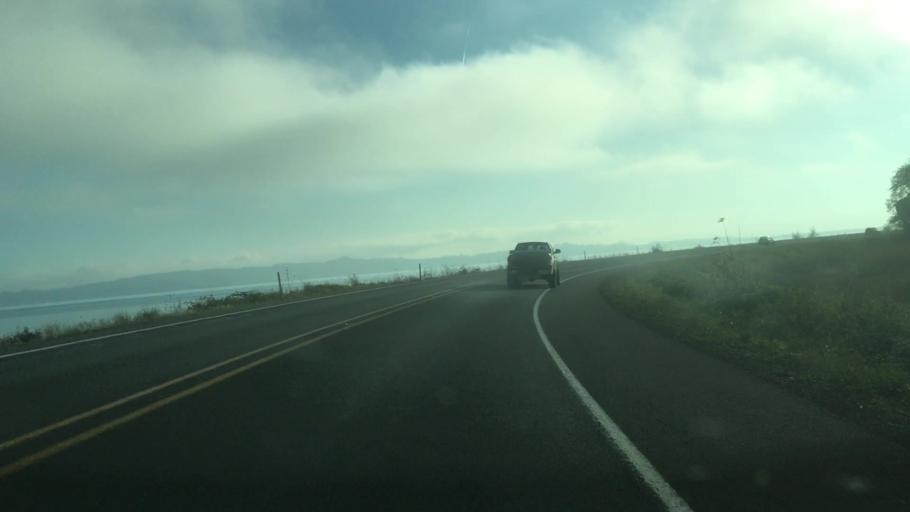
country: US
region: Oregon
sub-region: Clatsop County
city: Astoria
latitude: 46.2717
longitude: -123.8165
